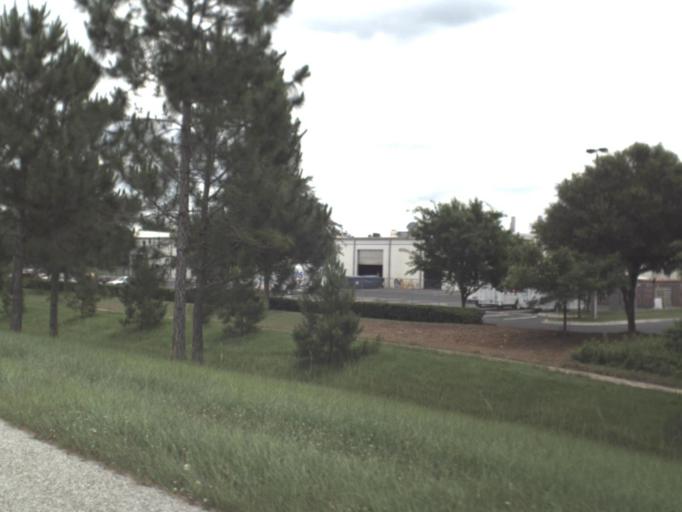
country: US
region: Florida
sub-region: Duval County
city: Jacksonville
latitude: 30.4714
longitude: -81.6650
